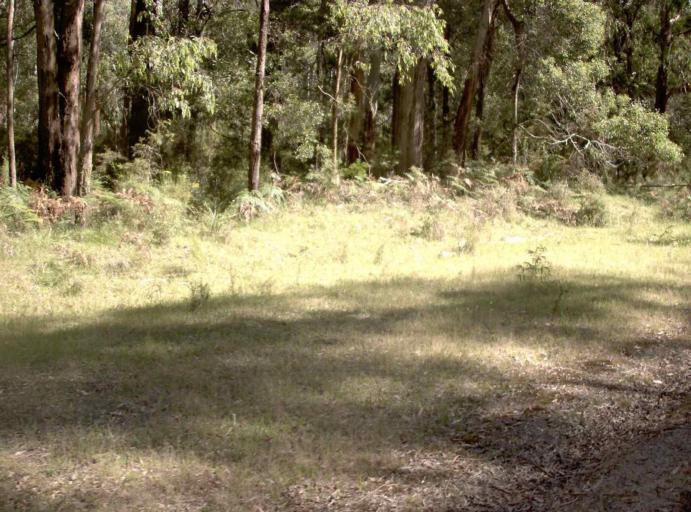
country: AU
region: New South Wales
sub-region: Bombala
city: Bombala
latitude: -37.3026
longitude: 148.7056
